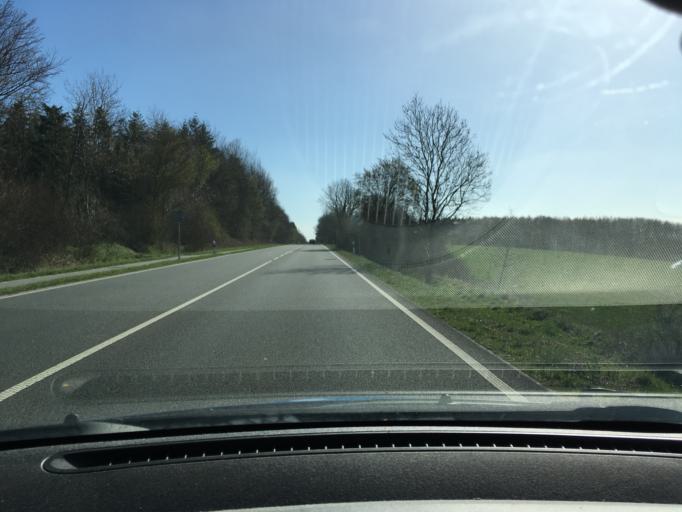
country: DE
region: Schleswig-Holstein
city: Fahrdorf
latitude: 54.4951
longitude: 9.6149
